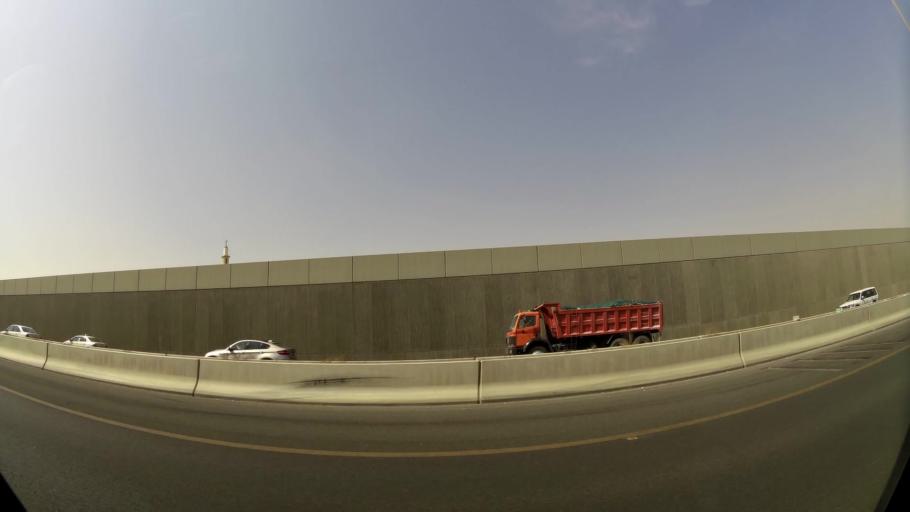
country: KW
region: Al Ahmadi
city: Al Manqaf
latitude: 29.1042
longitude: 48.1180
